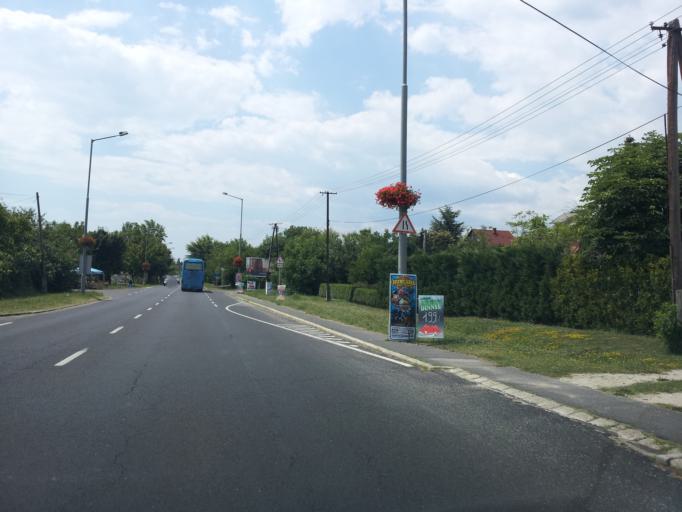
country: HU
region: Veszprem
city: Csopak
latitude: 46.9855
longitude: 17.9732
